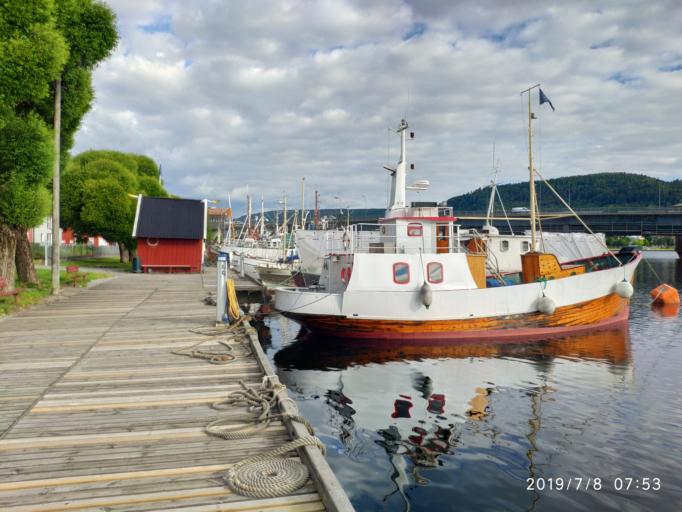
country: NO
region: Buskerud
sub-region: Drammen
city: Drammen
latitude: 59.7356
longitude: 10.2155
